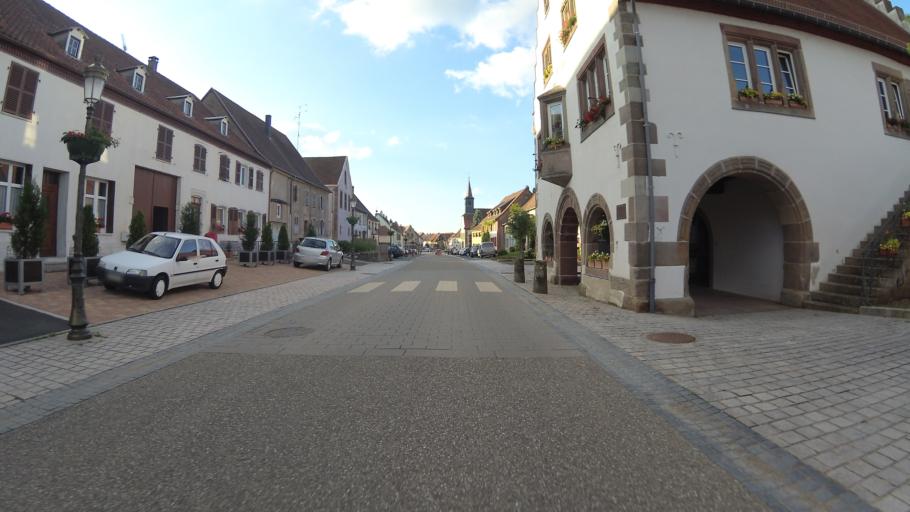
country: FR
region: Alsace
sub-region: Departement du Bas-Rhin
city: Oermingen
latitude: 48.9990
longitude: 7.1282
